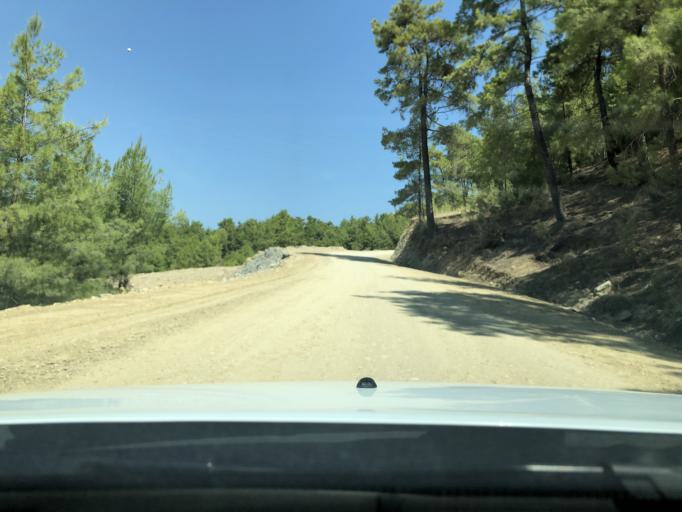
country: TR
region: Antalya
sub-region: Manavgat
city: Manavgat
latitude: 36.8338
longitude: 31.5334
